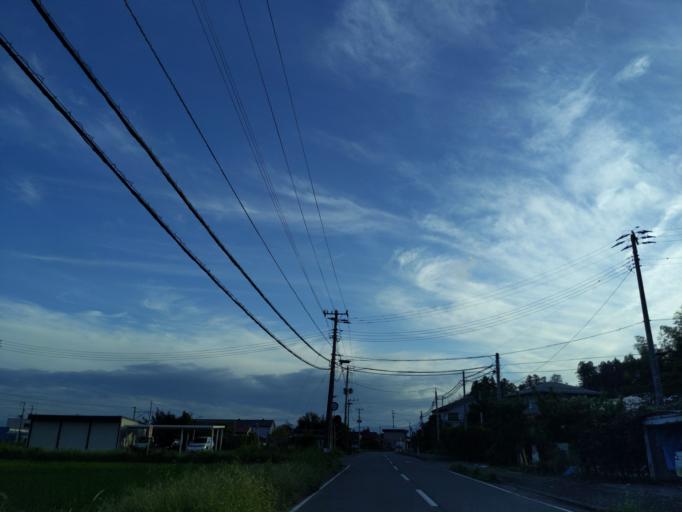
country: JP
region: Niigata
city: Kashiwazaki
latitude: 37.4370
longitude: 138.6256
